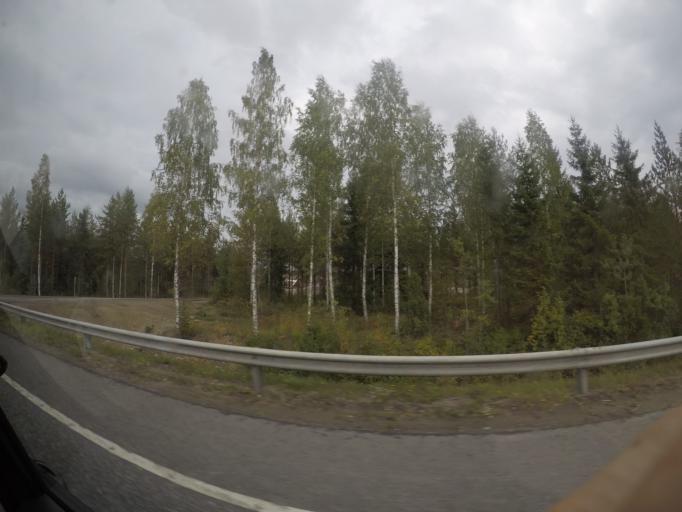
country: FI
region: Haeme
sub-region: Haemeenlinna
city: Parola
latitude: 61.1407
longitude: 24.4149
